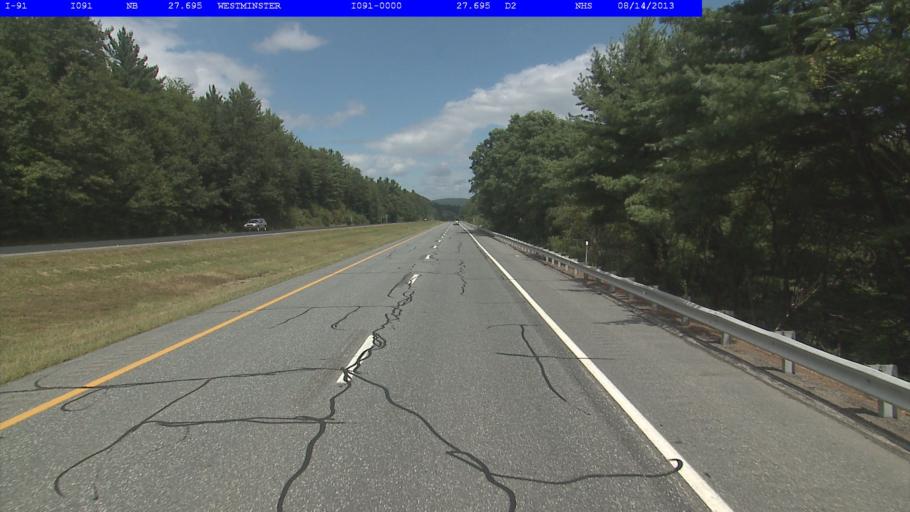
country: US
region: Vermont
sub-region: Windham County
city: Bellows Falls
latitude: 43.0790
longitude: -72.4640
